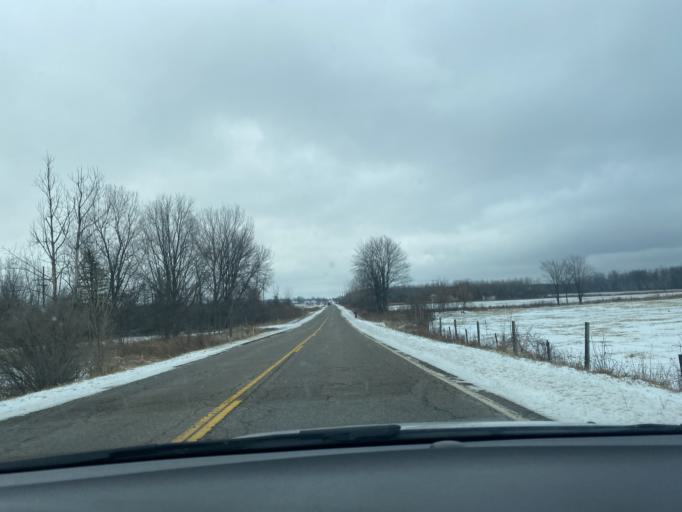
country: US
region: Michigan
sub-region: Lapeer County
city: North Branch
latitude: 43.2078
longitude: -83.1893
